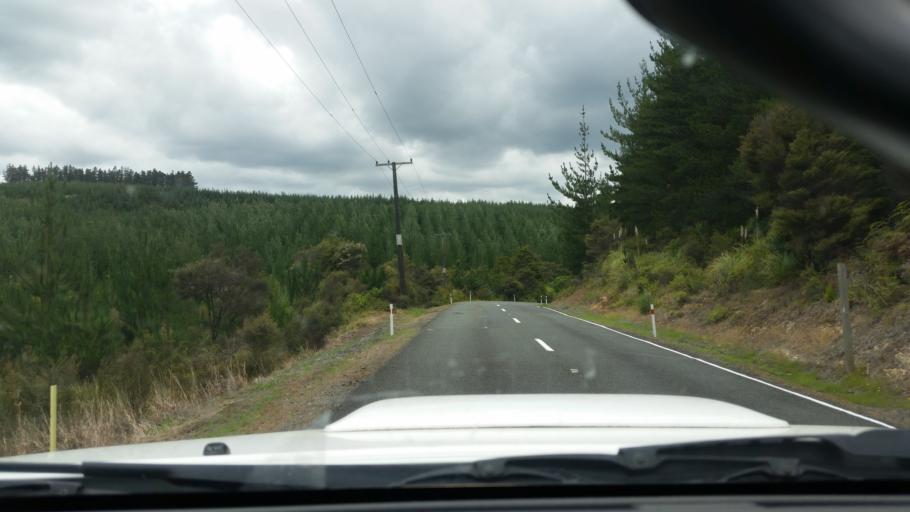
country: NZ
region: Northland
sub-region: Kaipara District
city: Dargaville
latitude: -35.8156
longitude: 173.7184
